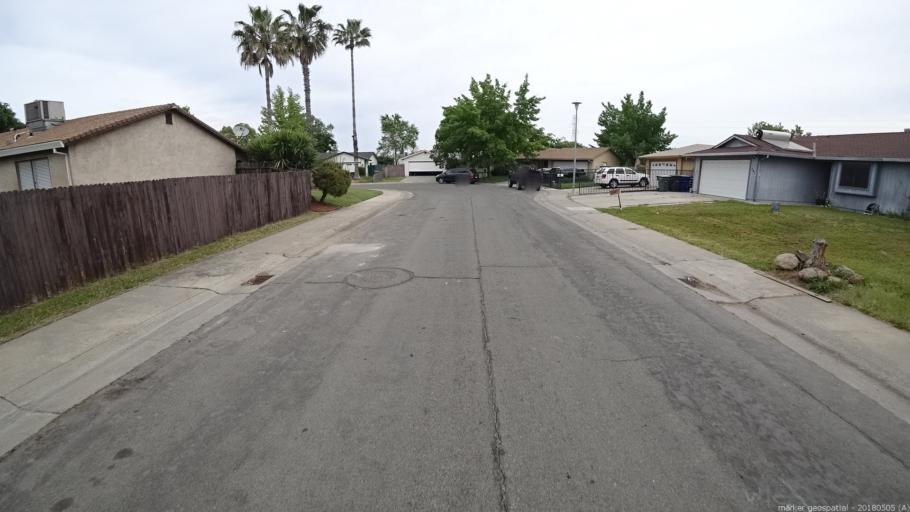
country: US
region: California
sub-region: Sacramento County
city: Rio Linda
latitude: 38.6451
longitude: -121.4493
